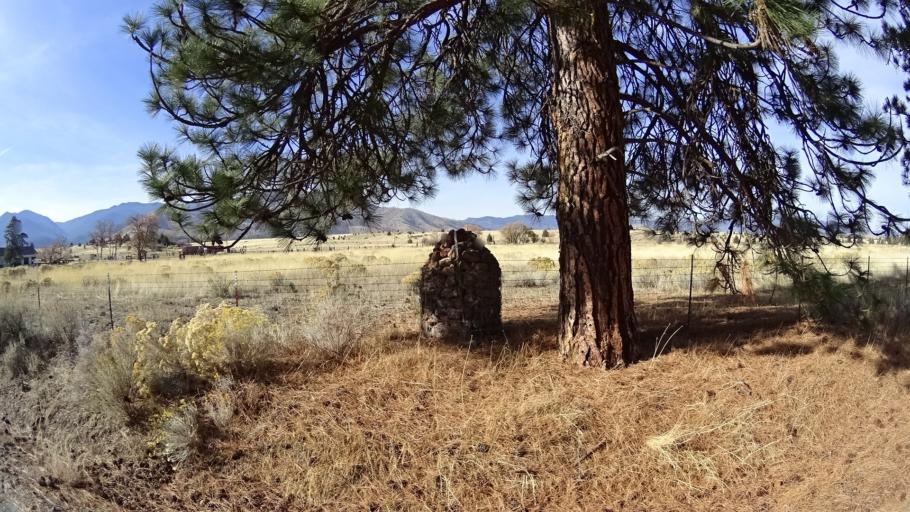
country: US
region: California
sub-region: Siskiyou County
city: Weed
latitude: 41.4839
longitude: -122.4432
